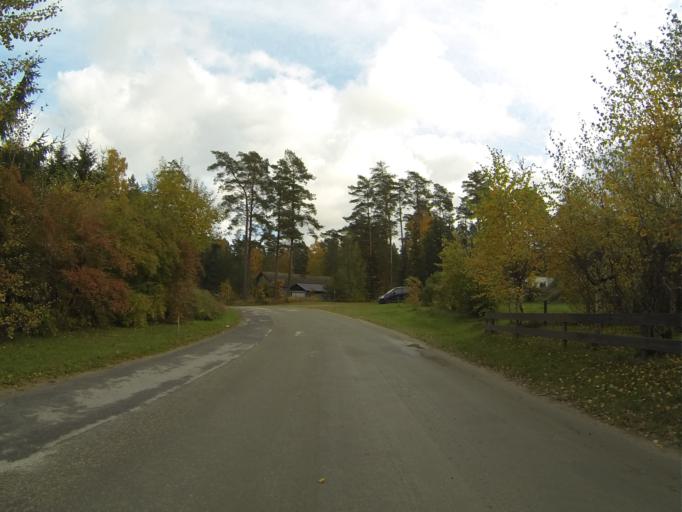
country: SE
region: Skane
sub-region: Sjobo Kommun
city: Sjoebo
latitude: 55.6332
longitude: 13.6535
